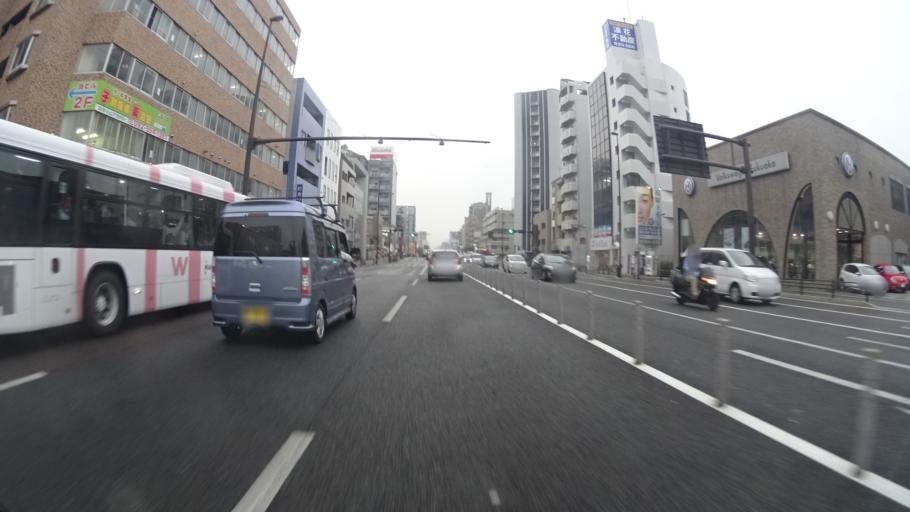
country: JP
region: Fukuoka
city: Fukuoka-shi
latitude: 33.5690
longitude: 130.4179
